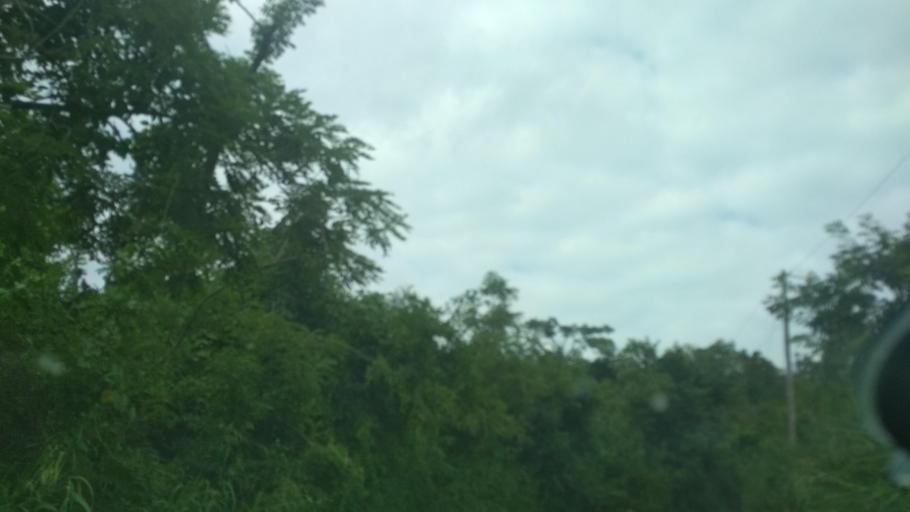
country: MX
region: Veracruz
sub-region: Poza Rica de Hidalgo
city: El Mollejon
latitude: 20.5213
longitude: -97.3799
